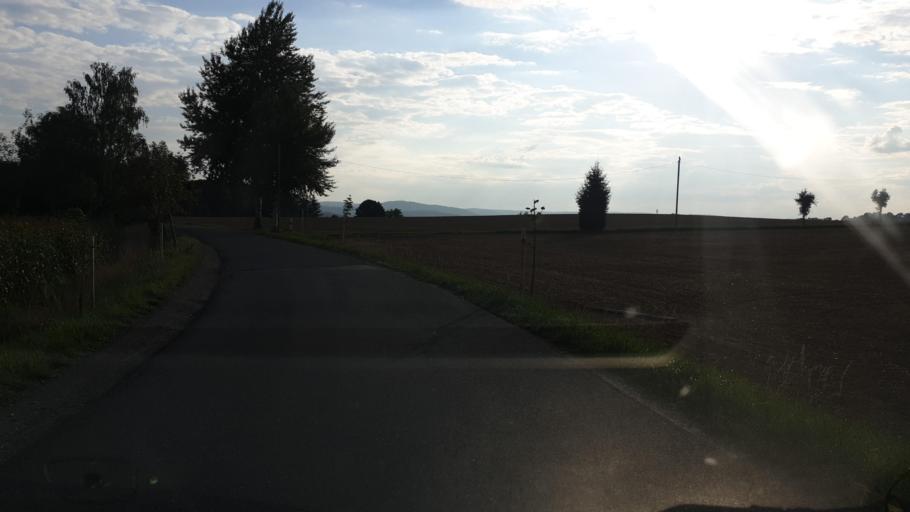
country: DE
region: Saxony
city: Lossnitz
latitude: 50.6261
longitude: 12.7461
